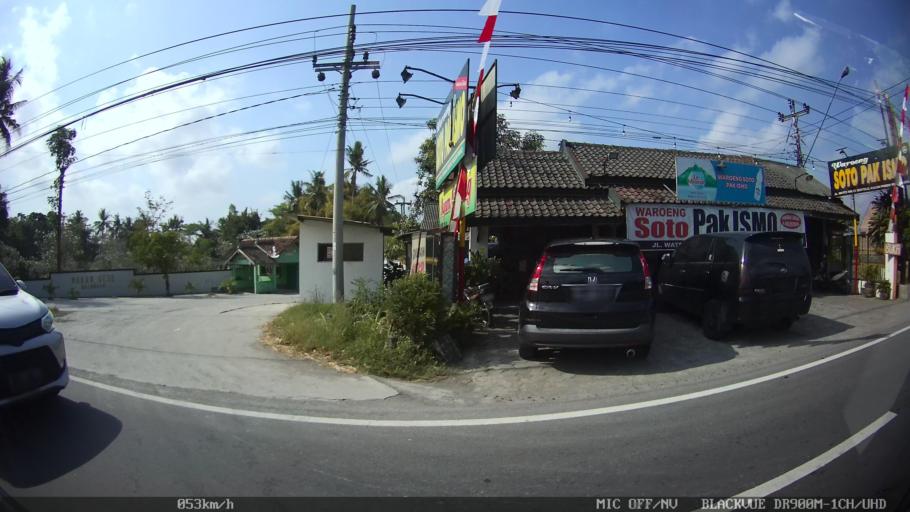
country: ID
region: Daerah Istimewa Yogyakarta
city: Godean
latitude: -7.8243
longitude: 110.2308
